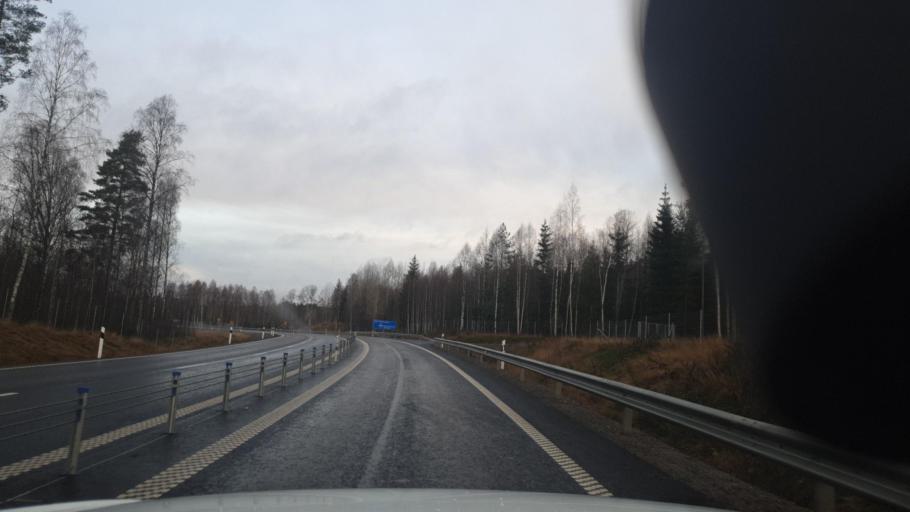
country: SE
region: Vaermland
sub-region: Arvika Kommun
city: Arvika
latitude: 59.7051
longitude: 12.5758
